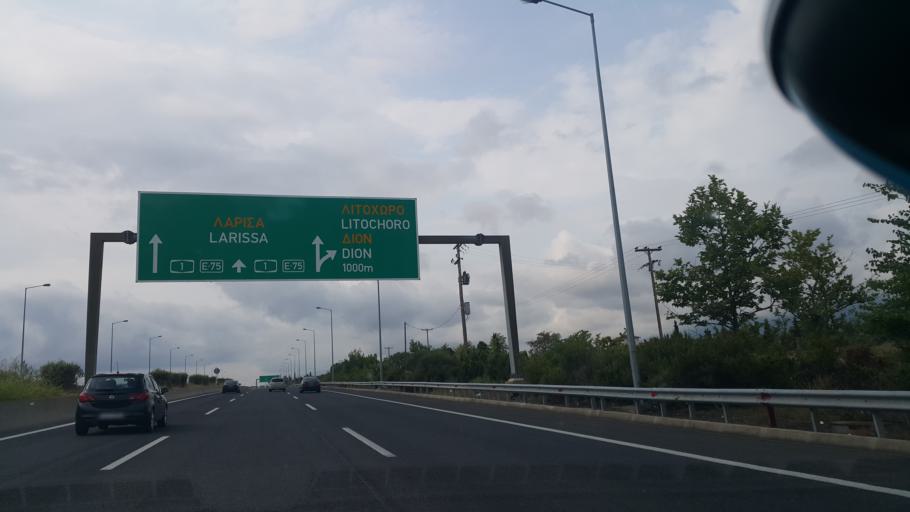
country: GR
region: Central Macedonia
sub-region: Nomos Pierias
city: Litochoro
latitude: 40.1419
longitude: 22.5428
